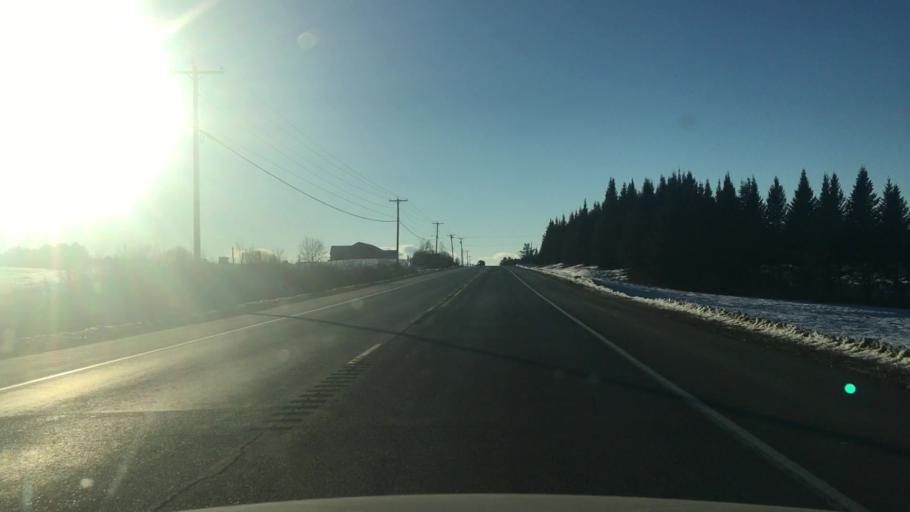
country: US
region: Maine
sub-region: Somerset County
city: Norridgewock
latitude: 44.7038
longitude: -69.8244
